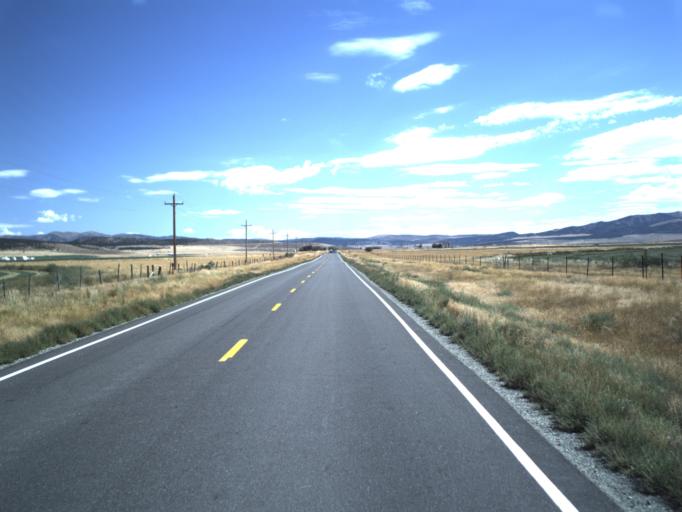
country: US
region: Idaho
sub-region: Oneida County
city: Malad City
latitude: 41.9674
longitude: -112.8282
